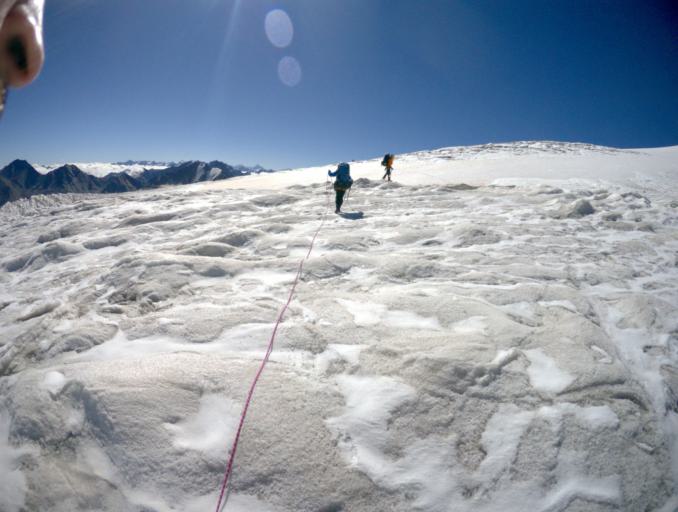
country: RU
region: Kabardino-Balkariya
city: Terskol
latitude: 43.3655
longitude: 42.4961
